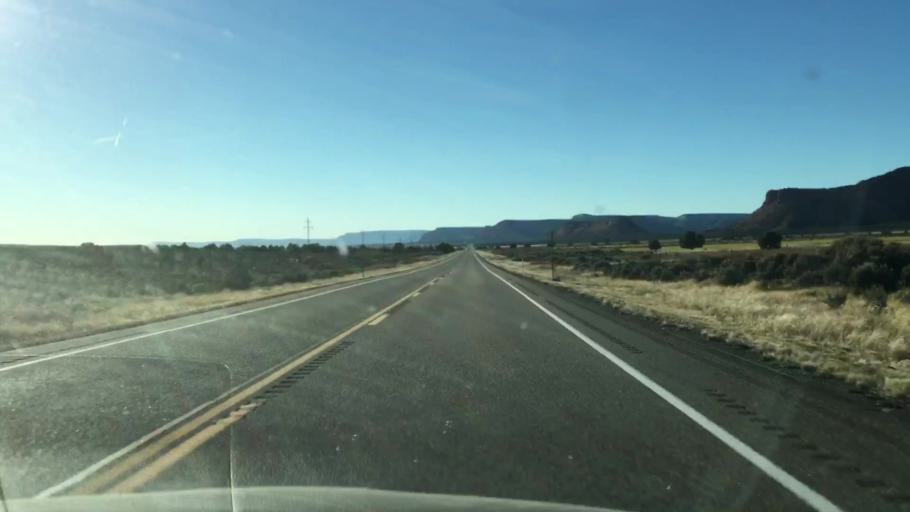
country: US
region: Utah
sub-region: Kane County
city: Kanab
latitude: 37.0395
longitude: -112.2886
